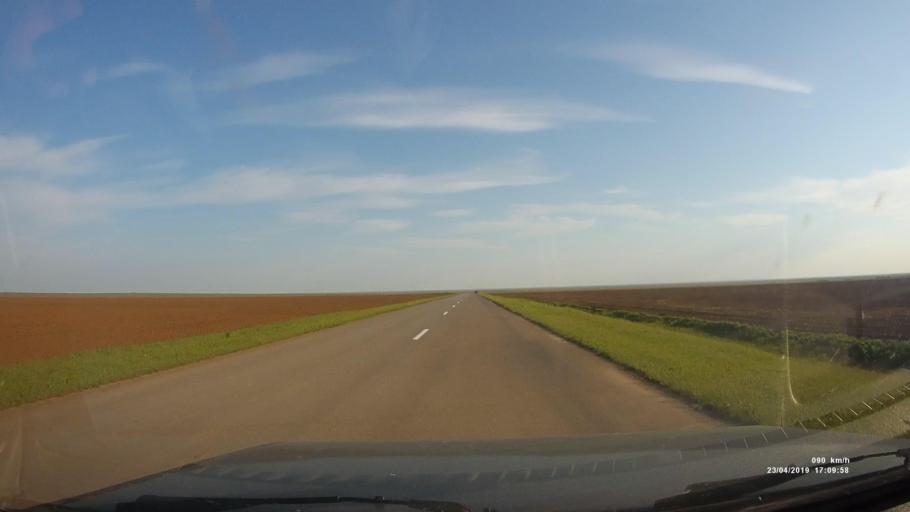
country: RU
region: Kalmykiya
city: Priyutnoye
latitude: 46.2509
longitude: 43.4842
